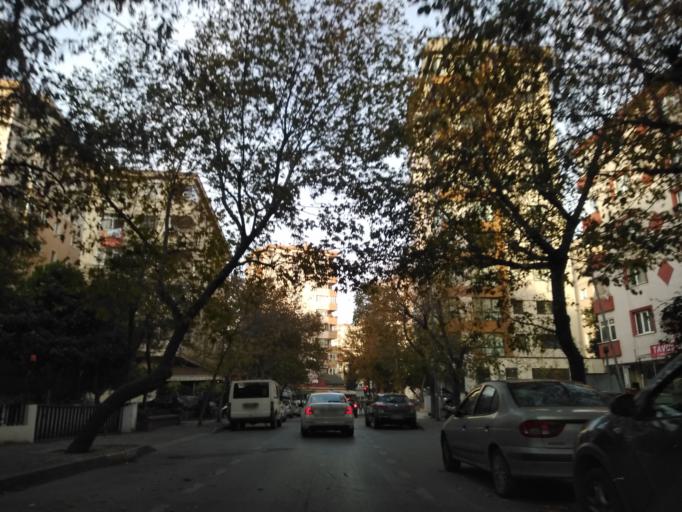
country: TR
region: Istanbul
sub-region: Atasehir
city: Atasehir
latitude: 40.9779
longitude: 29.0913
